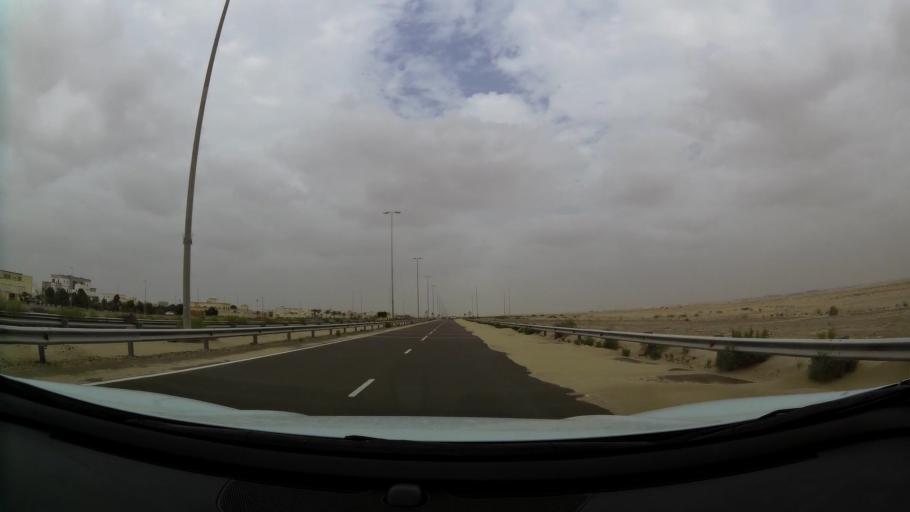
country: AE
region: Abu Dhabi
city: Abu Dhabi
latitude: 24.3447
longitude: 54.6573
